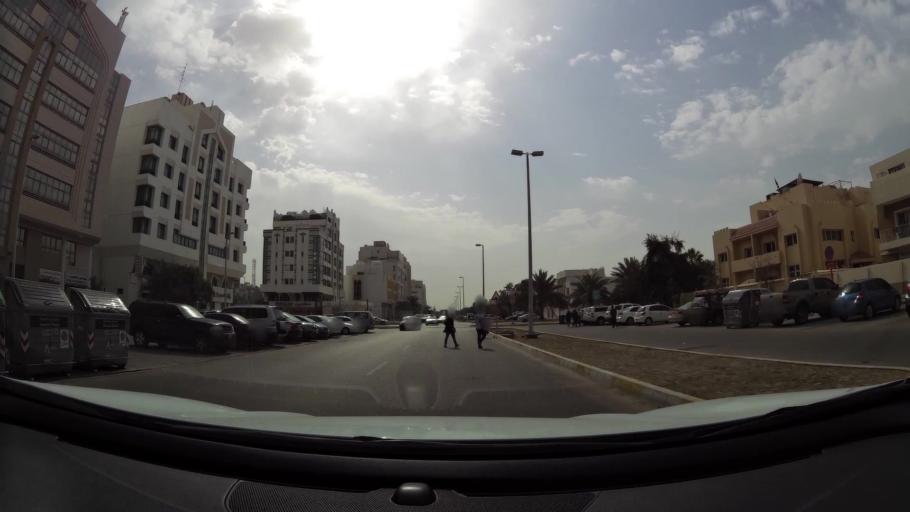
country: AE
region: Abu Dhabi
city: Abu Dhabi
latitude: 24.4521
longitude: 54.3864
